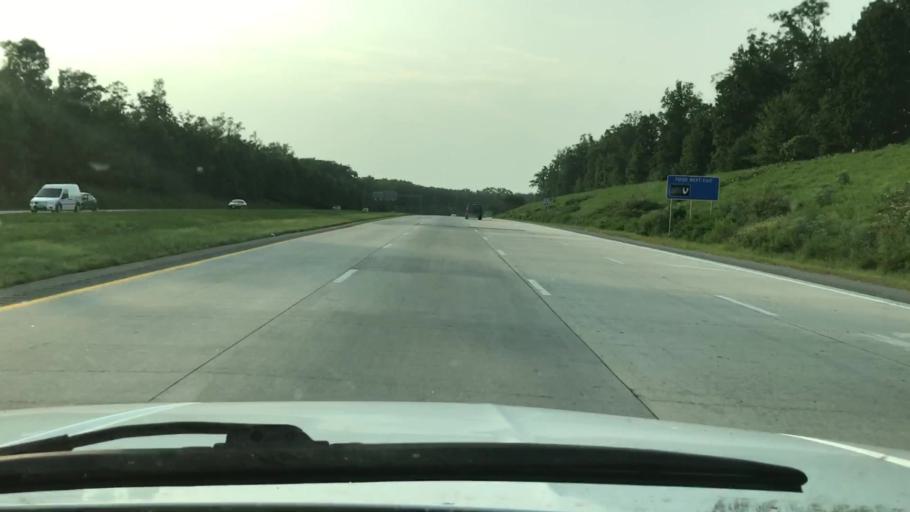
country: US
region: Virginia
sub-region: Chesterfield County
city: Brandermill
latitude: 37.4733
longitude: -77.6555
